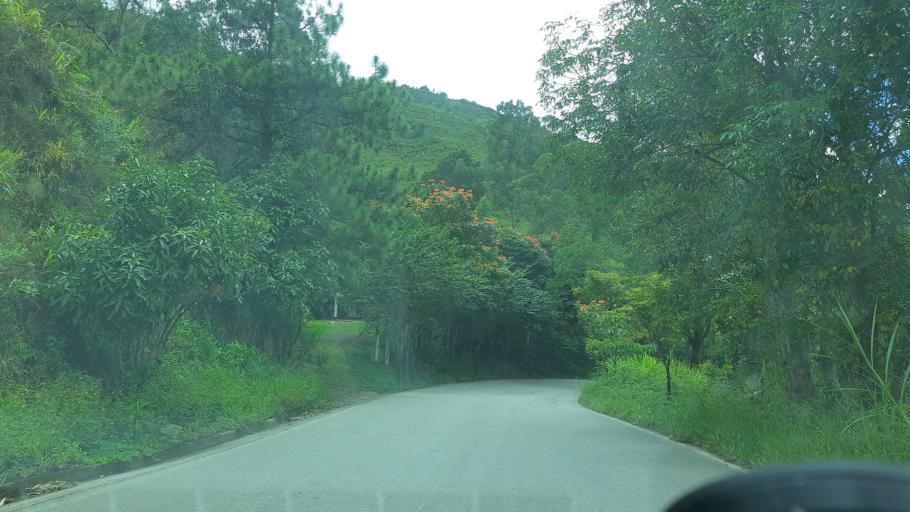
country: CO
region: Boyaca
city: Garagoa
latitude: 5.0509
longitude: -73.3871
